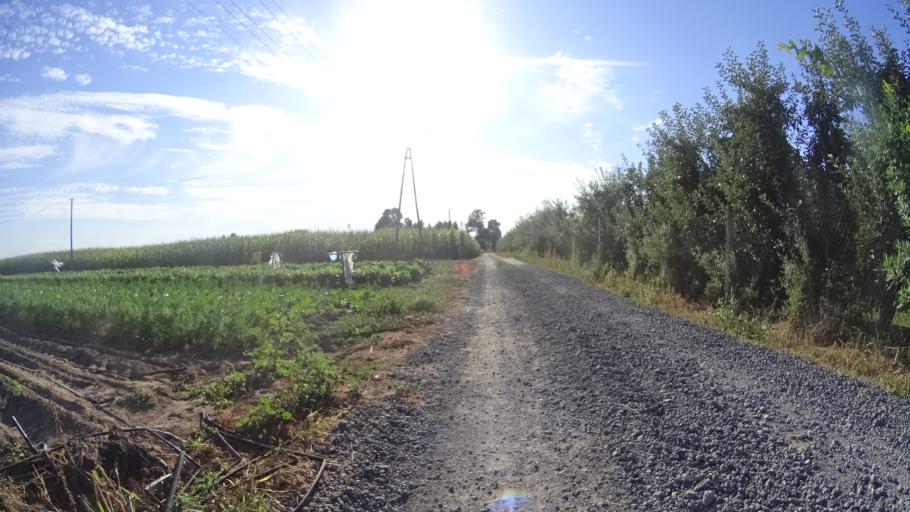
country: PL
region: Masovian Voivodeship
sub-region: Powiat bialobrzeski
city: Wysmierzyce
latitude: 51.6737
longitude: 20.8350
